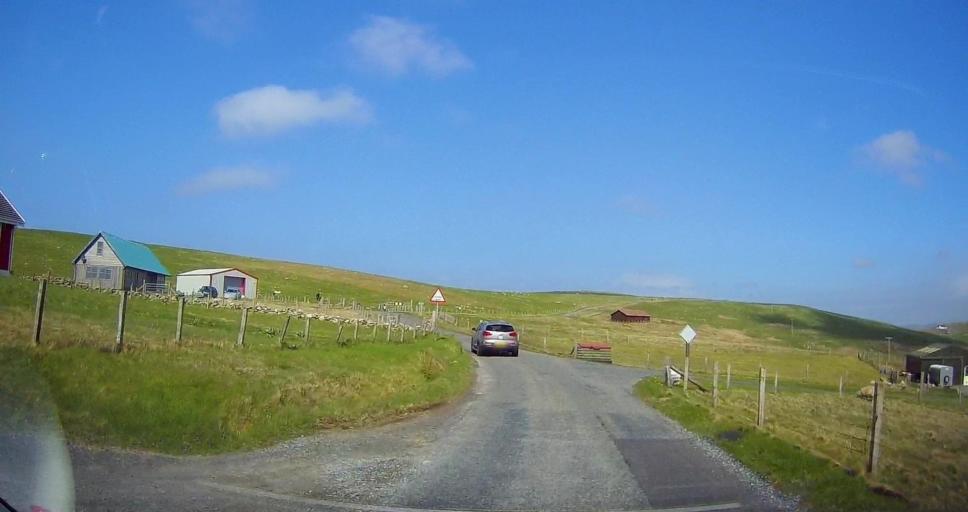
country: GB
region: Scotland
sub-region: Shetland Islands
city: Sandwick
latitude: 60.0696
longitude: -1.3399
